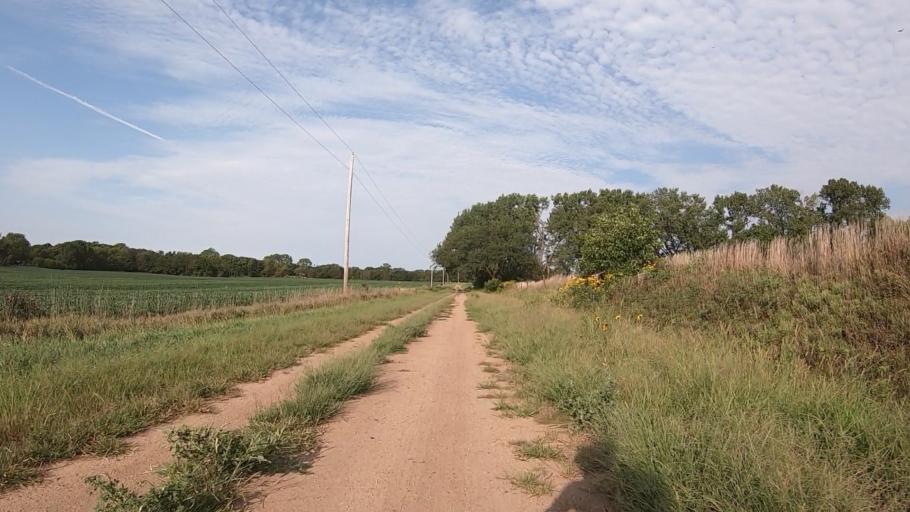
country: US
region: Kansas
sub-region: Washington County
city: Washington
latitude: 39.6714
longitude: -96.9437
